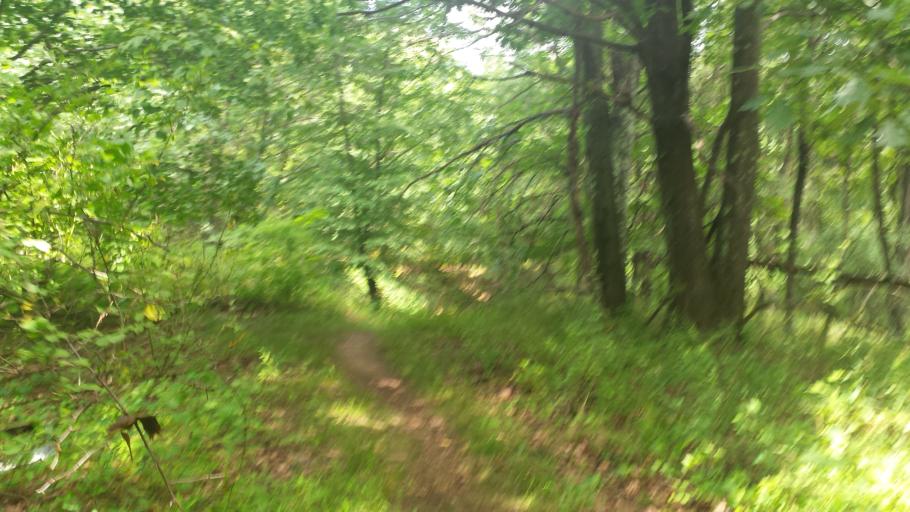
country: US
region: New York
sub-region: Westchester County
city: Thornwood
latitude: 41.1200
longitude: -73.7910
